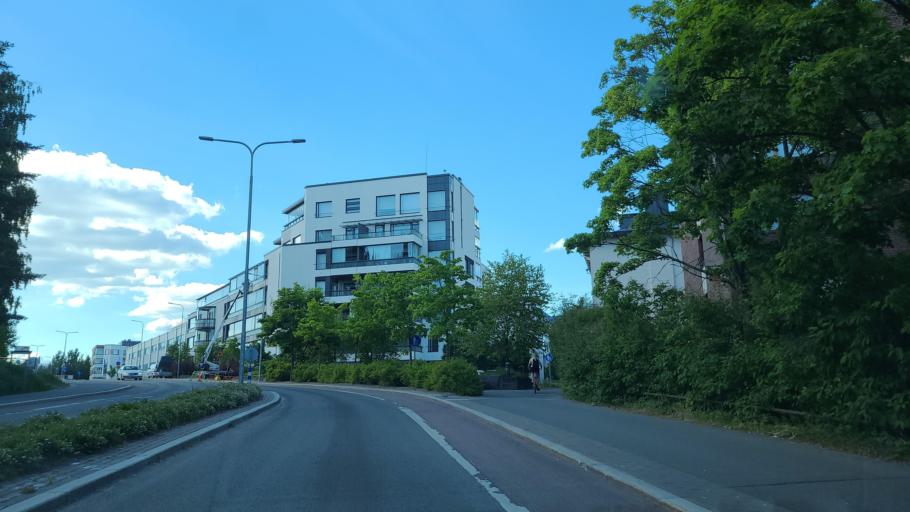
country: FI
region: Central Finland
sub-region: Jyvaeskylae
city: Jyvaeskylae
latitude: 62.2463
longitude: 25.7438
